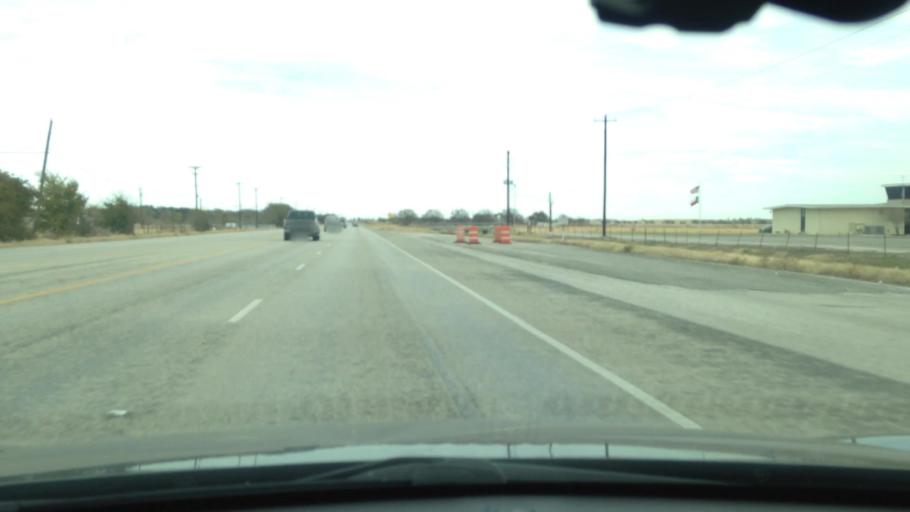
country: US
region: Texas
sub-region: Caldwell County
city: Martindale
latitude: 29.9022
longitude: -97.8682
